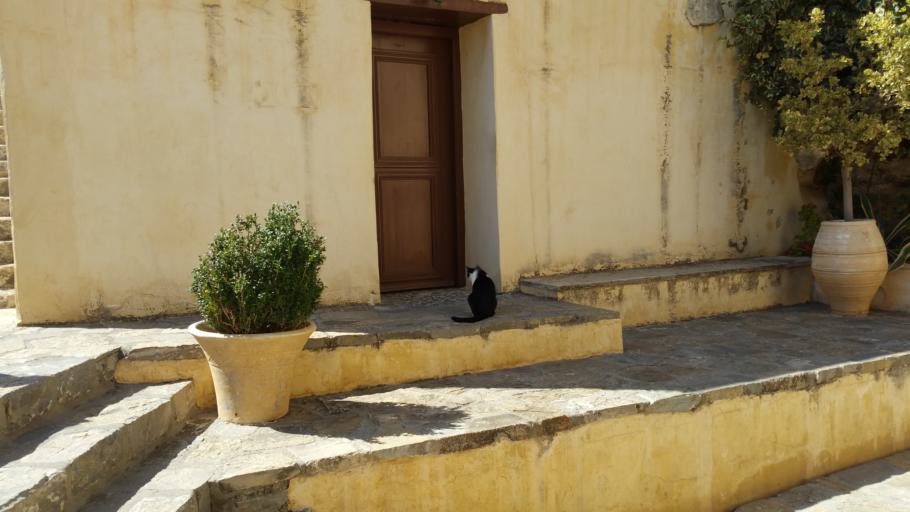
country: GR
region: Crete
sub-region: Nomos Rethymnis
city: Atsipopoulon
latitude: 35.1576
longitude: 24.4565
